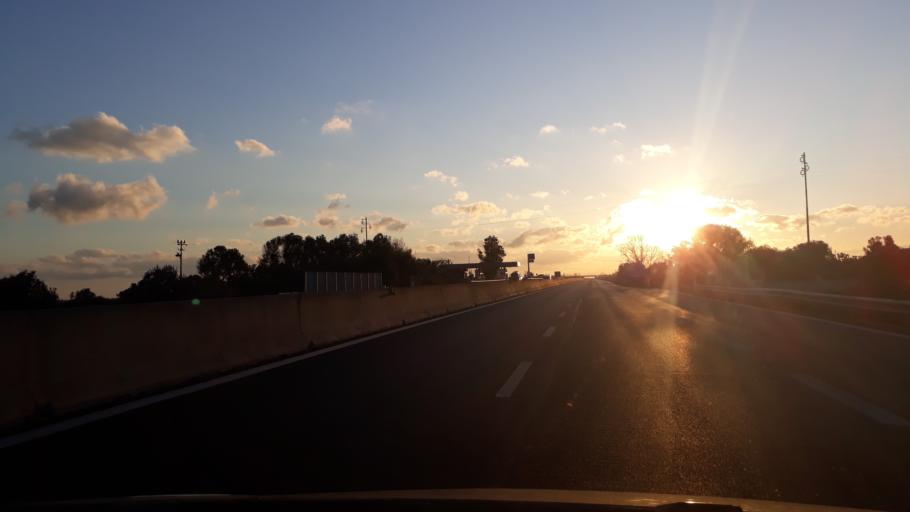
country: IT
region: Apulia
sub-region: Provincia di Brindisi
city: Ostuni
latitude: 40.7781
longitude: 17.6029
